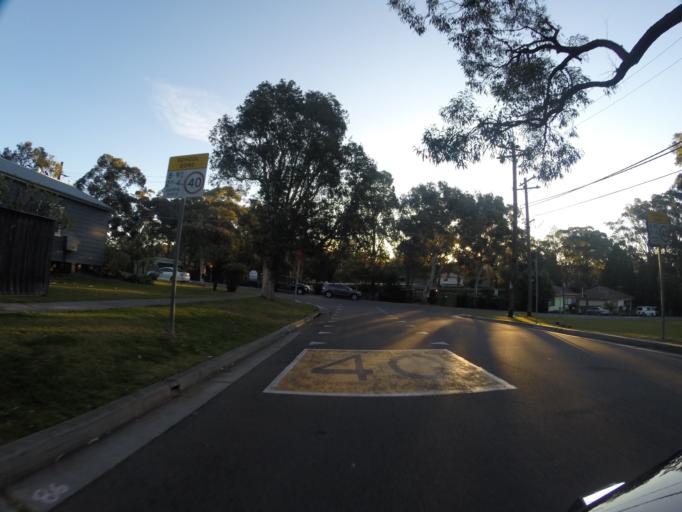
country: AU
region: New South Wales
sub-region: Sutherland Shire
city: Gymea
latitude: -34.0373
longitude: 151.0885
